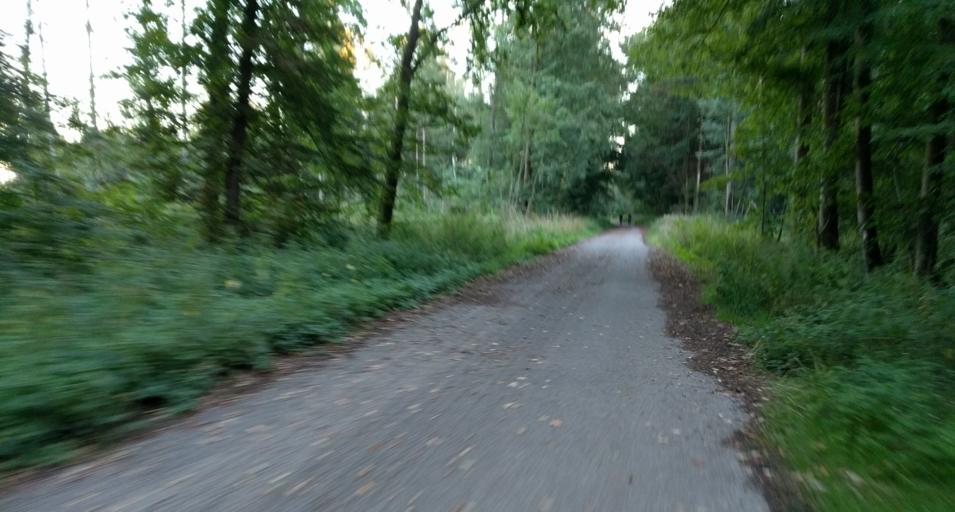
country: DE
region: Bavaria
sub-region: Upper Bavaria
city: Oberhaching
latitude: 48.0265
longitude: 11.5673
